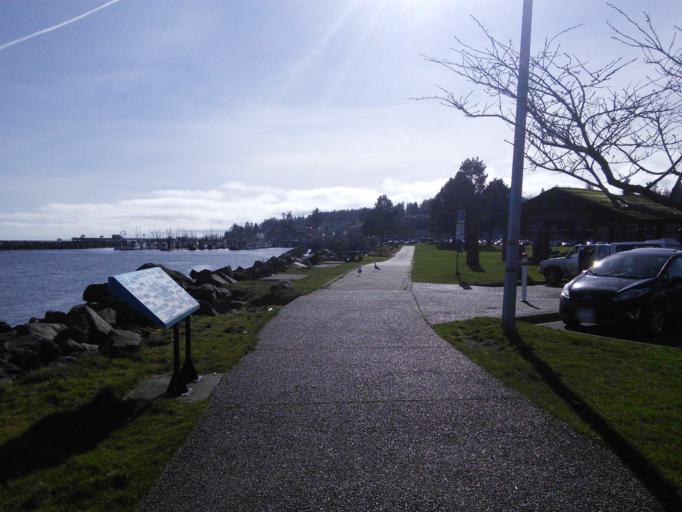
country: CA
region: British Columbia
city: Campbell River
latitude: 50.0267
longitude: -125.2403
